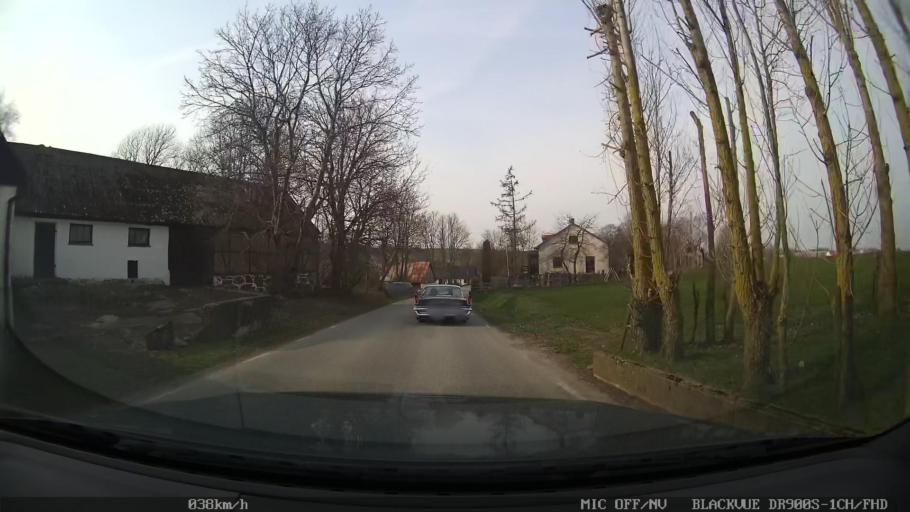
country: SE
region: Skane
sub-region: Ystads Kommun
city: Ystad
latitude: 55.4635
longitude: 13.8230
